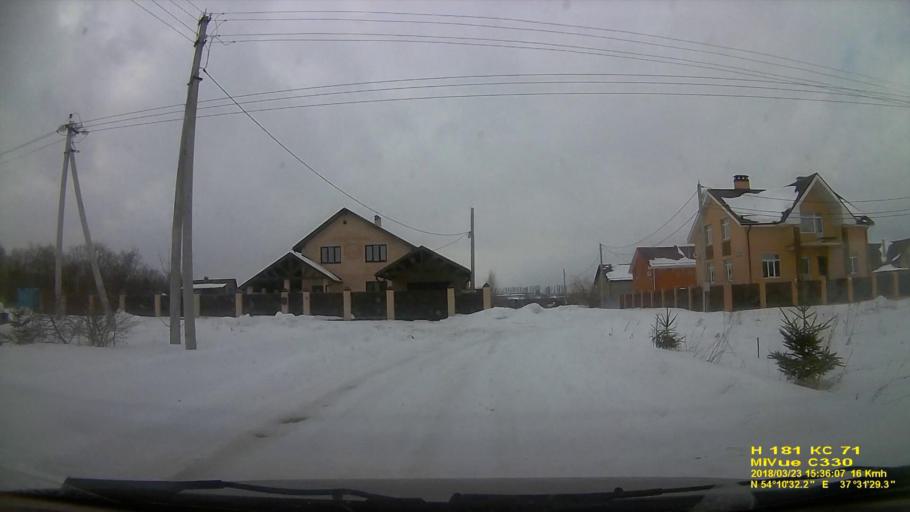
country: RU
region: Tula
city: Kosaya Gora
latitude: 54.1757
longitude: 37.5247
